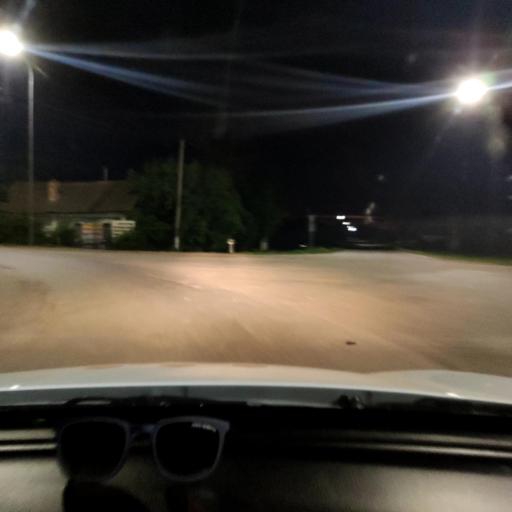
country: RU
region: Tatarstan
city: Rybnaya Sloboda
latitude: 55.4804
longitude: 50.1332
